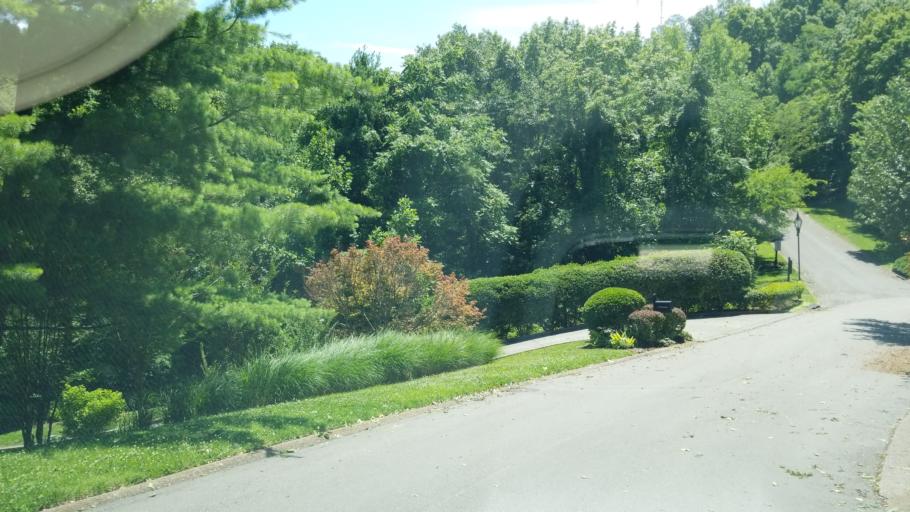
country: US
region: Tennessee
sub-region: Davidson County
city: Forest Hills
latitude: 36.0515
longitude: -86.8262
